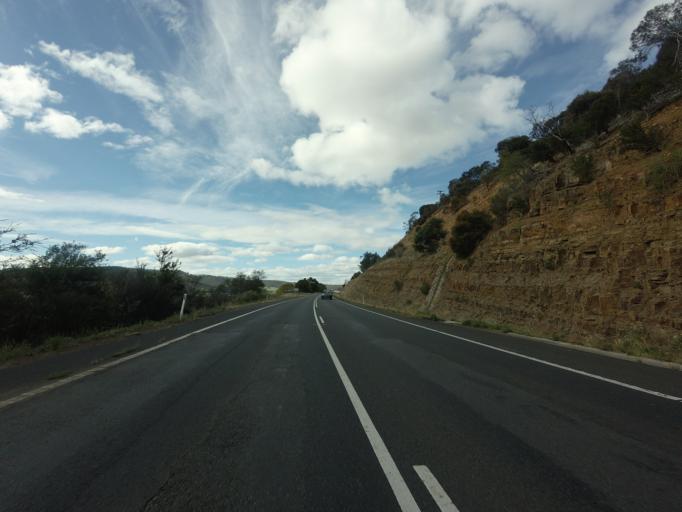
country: AU
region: Tasmania
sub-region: Glenorchy
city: Granton
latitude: -42.7472
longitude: 147.1777
